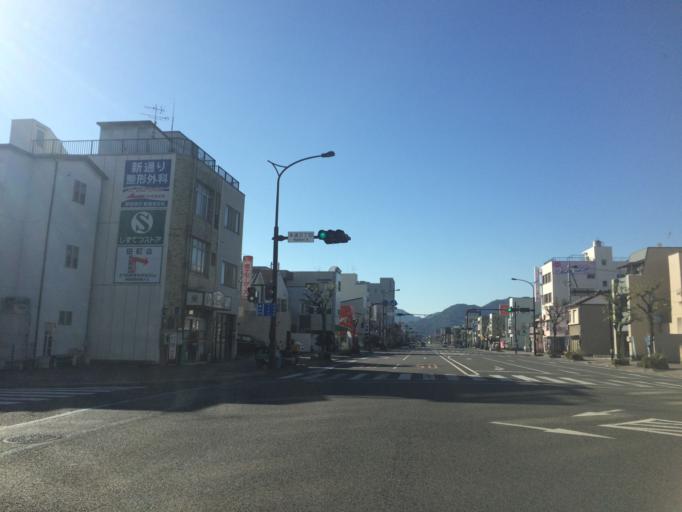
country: JP
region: Shizuoka
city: Shizuoka-shi
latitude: 34.9690
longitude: 138.3742
